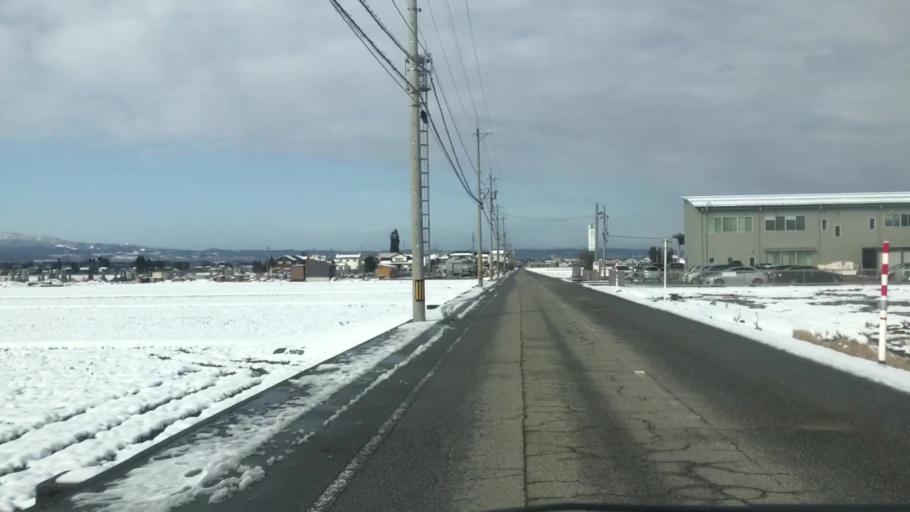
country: JP
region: Toyama
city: Toyama-shi
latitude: 36.6125
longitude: 137.2685
